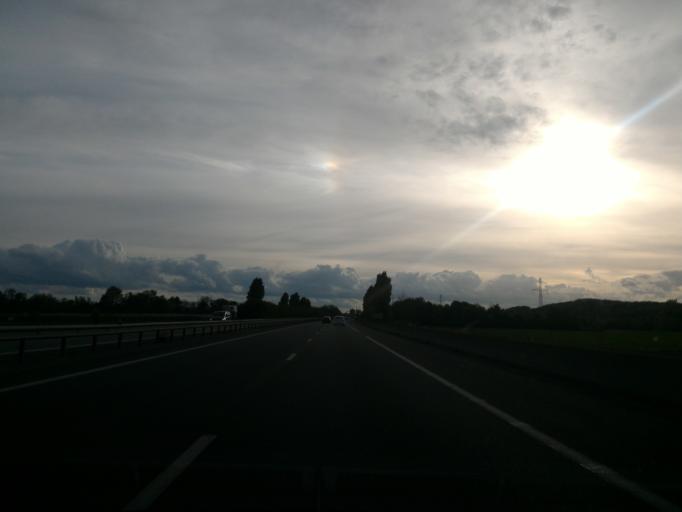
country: FR
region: Alsace
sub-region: Departement du Haut-Rhin
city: Heimsbrunn
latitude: 47.7320
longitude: 7.1964
